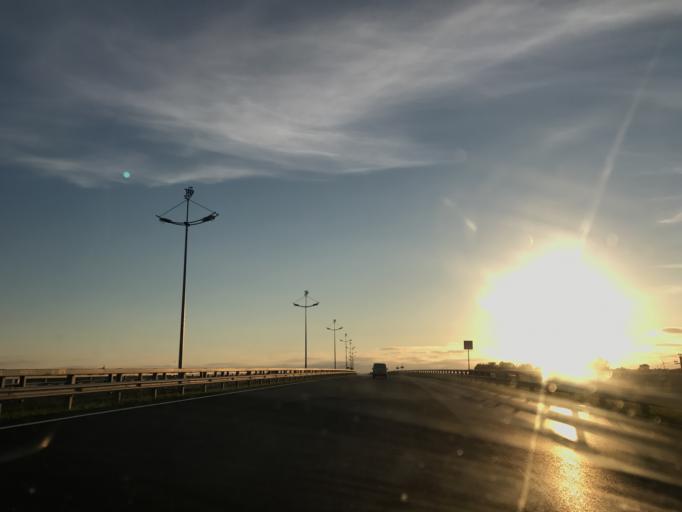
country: RU
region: Kaliningrad
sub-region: Zelenogradskiy Rayon
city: Zelenogradsk
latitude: 54.9226
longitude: 20.4045
